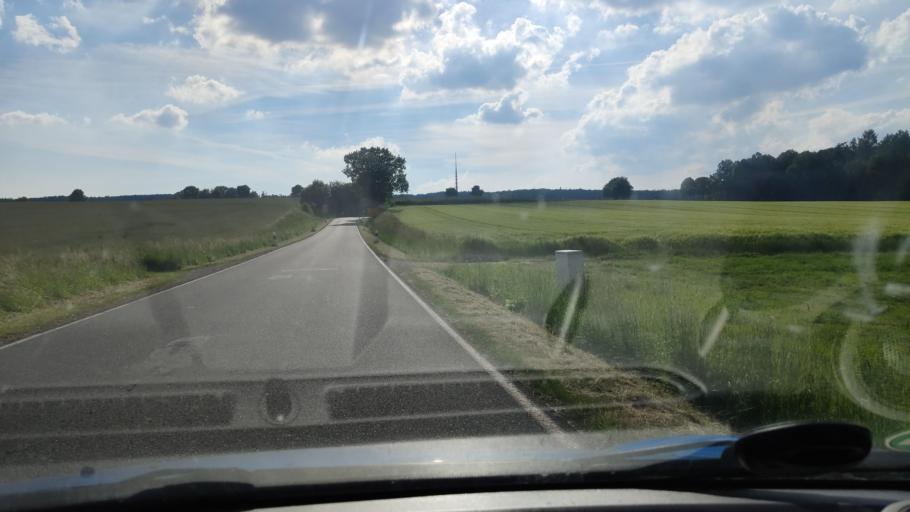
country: DE
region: Lower Saxony
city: Hardegsen
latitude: 51.7094
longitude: 9.7885
